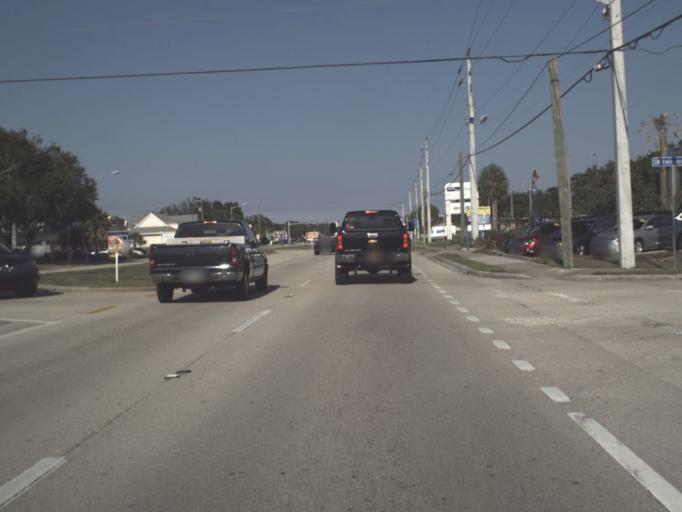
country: US
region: Florida
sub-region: Brevard County
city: West Melbourne
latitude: 28.0787
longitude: -80.6415
